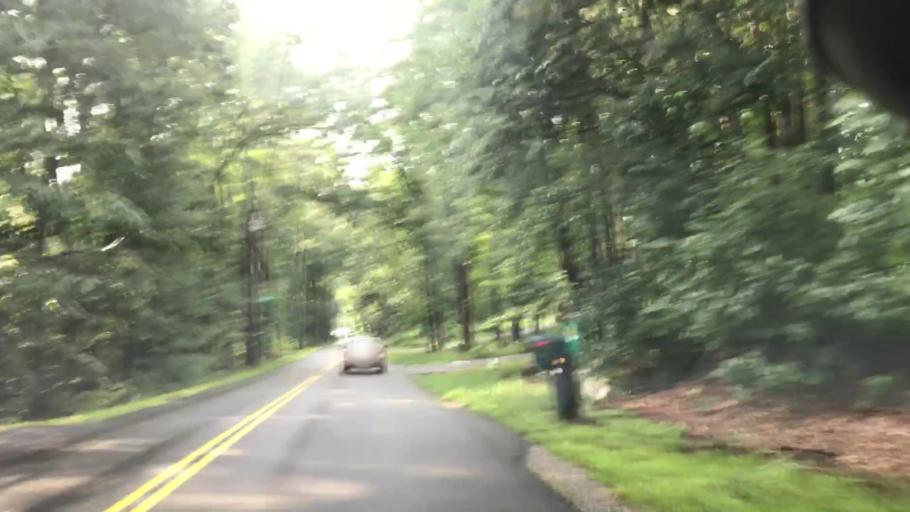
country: US
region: New Hampshire
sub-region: Hillsborough County
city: Milford
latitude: 42.8436
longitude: -71.6074
